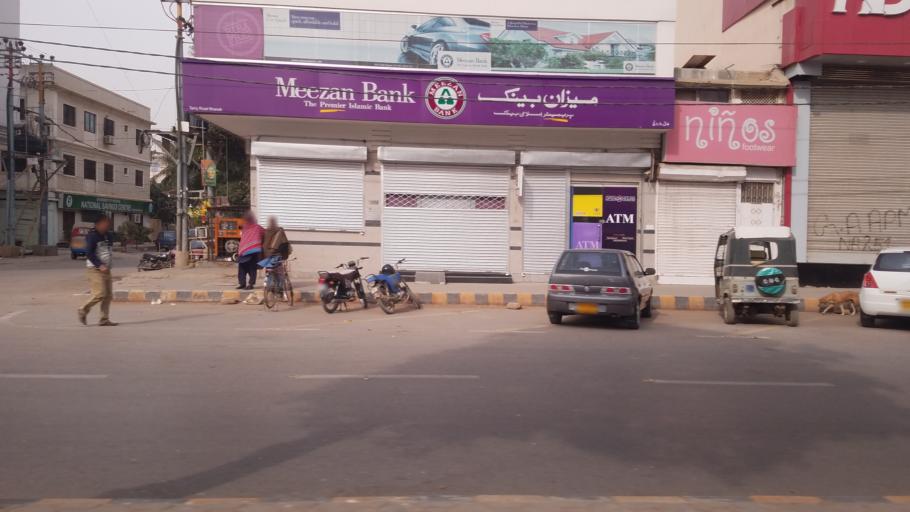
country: PK
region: Sindh
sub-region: Karachi District
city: Karachi
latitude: 24.8694
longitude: 67.0584
